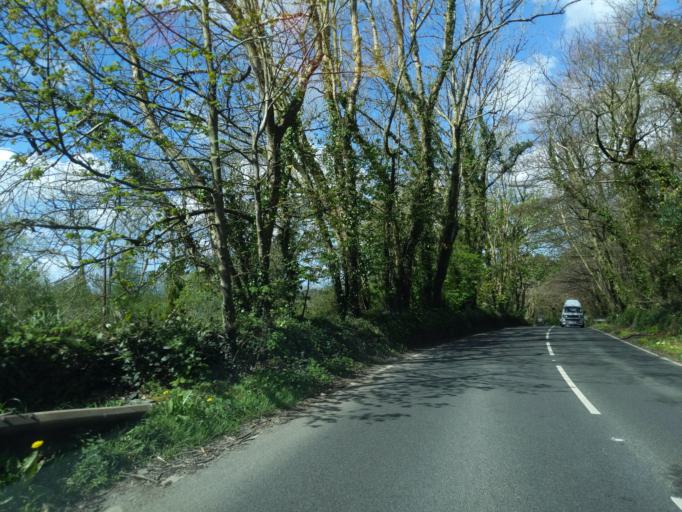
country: GB
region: England
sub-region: Cornwall
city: Bodmin
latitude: 50.4983
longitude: -4.7755
